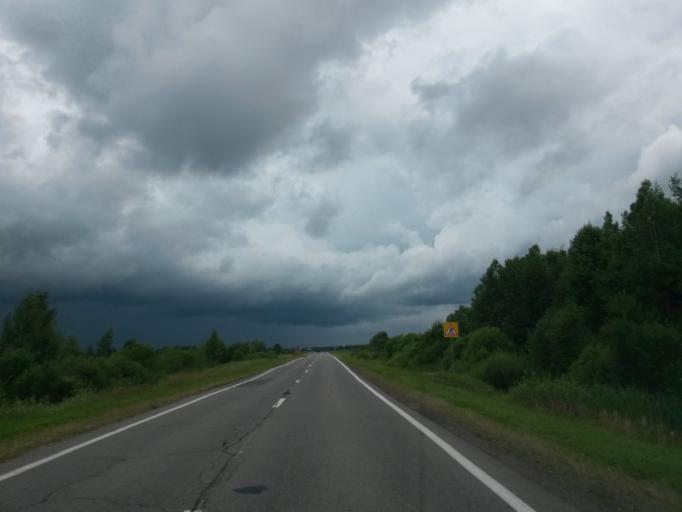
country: RU
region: Jaroslavl
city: Konstantinovskiy
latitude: 57.8675
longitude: 39.6031
